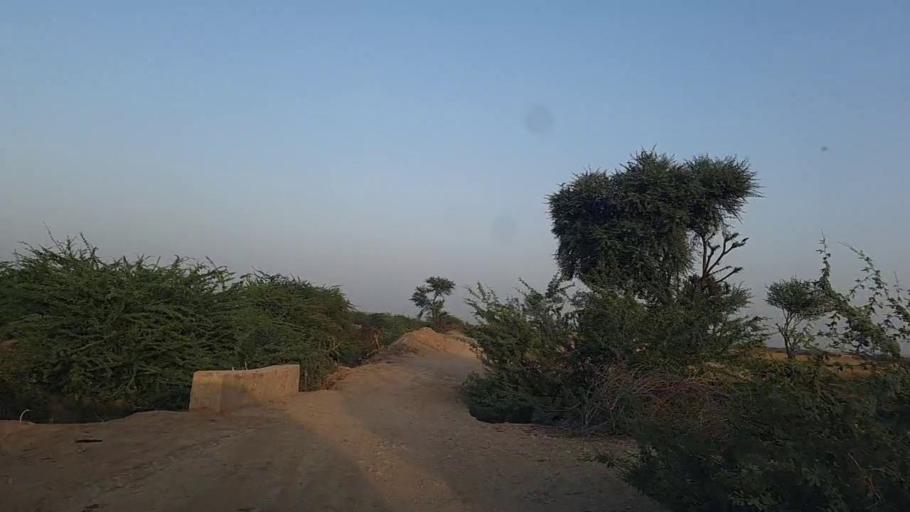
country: PK
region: Sindh
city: Naukot
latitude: 24.6975
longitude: 69.2612
